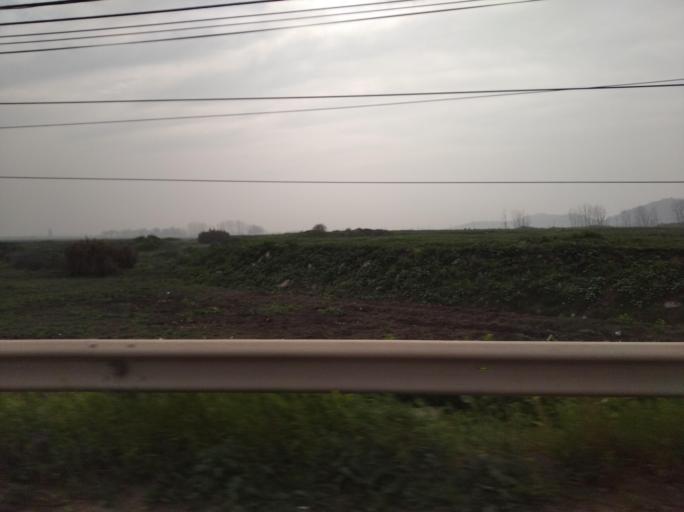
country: CL
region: Santiago Metropolitan
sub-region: Provincia de Chacabuco
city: Lampa
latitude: -33.3471
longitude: -70.8072
